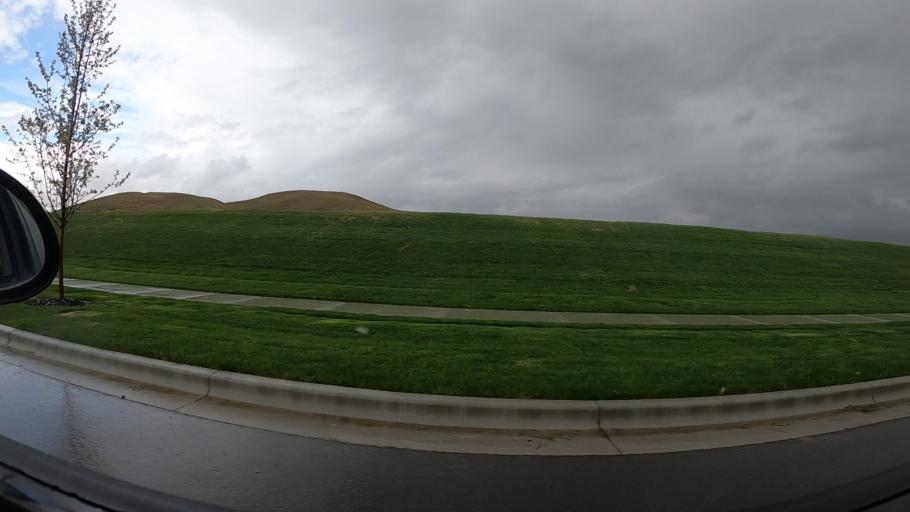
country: US
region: Idaho
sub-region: Ada County
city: Eagle
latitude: 43.7354
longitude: -116.2835
